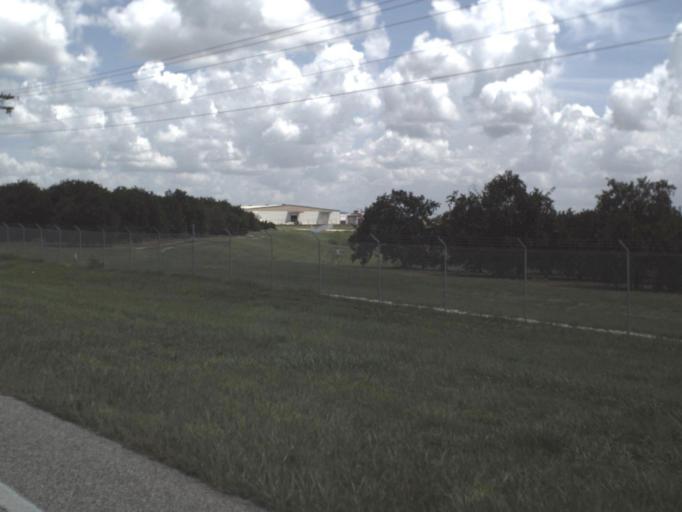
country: US
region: Florida
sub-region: Polk County
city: Eagle Lake
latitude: 27.9465
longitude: -81.7946
